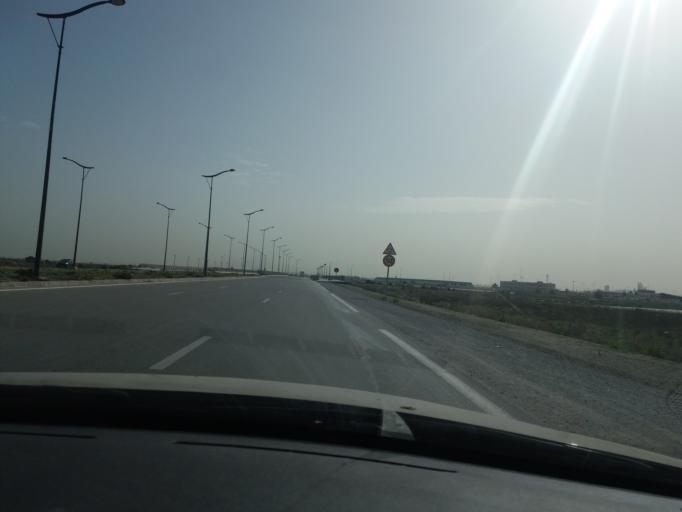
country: TN
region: Tunis
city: Tunis
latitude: 36.8062
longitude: 10.1945
